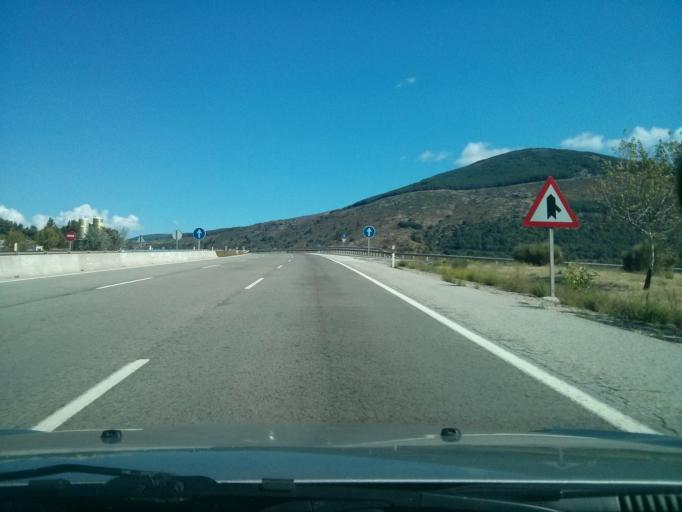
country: ES
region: Madrid
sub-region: Provincia de Madrid
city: Robregordo
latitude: 41.0960
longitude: -3.5936
